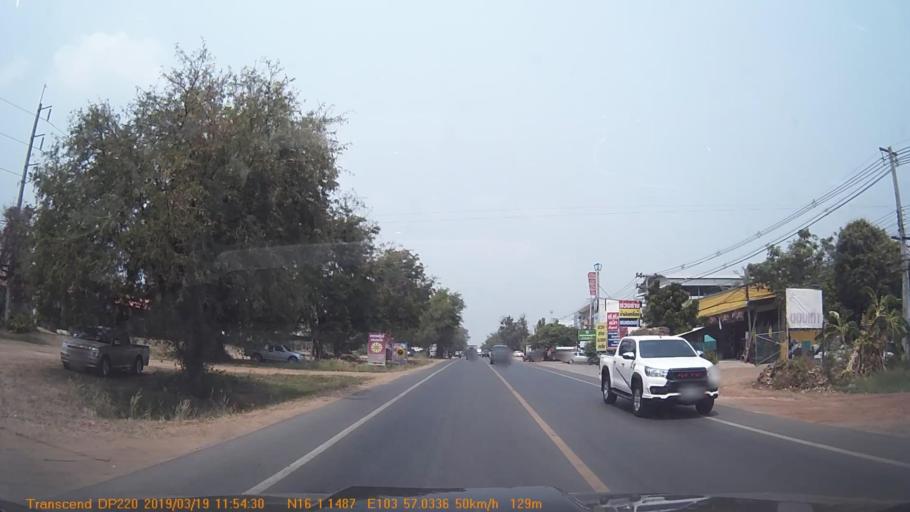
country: TH
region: Roi Et
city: Ban Selaphum
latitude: 16.0192
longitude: 103.9505
